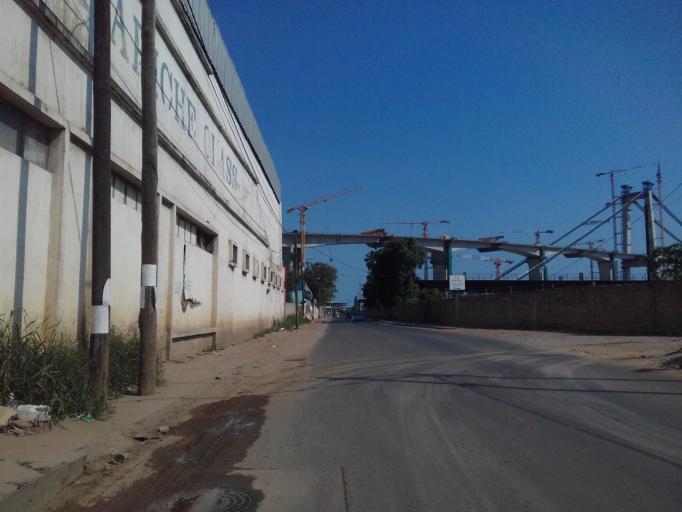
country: MZ
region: Maputo City
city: Maputo
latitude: -25.9633
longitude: 32.5577
